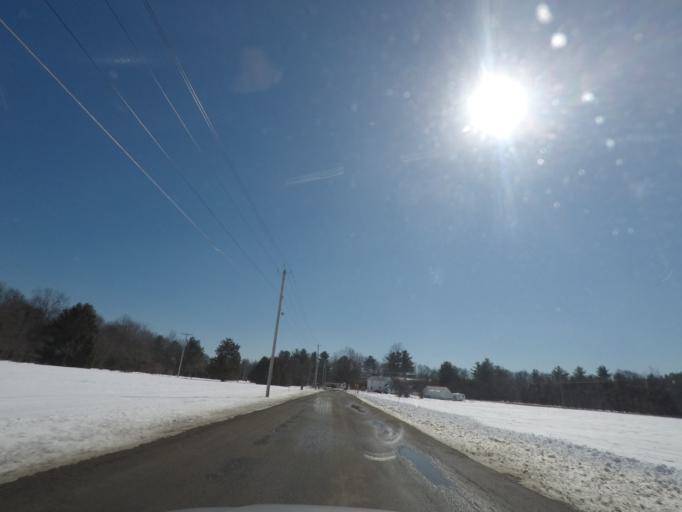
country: US
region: New York
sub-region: Saratoga County
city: Stillwater
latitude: 42.9089
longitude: -73.6064
